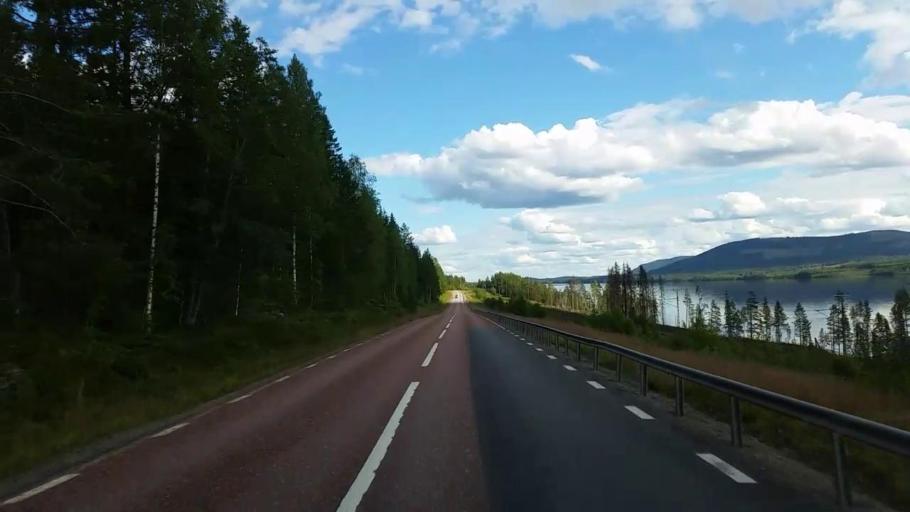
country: SE
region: Gaevleborg
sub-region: Ljusdals Kommun
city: Farila
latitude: 62.1084
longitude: 15.7702
